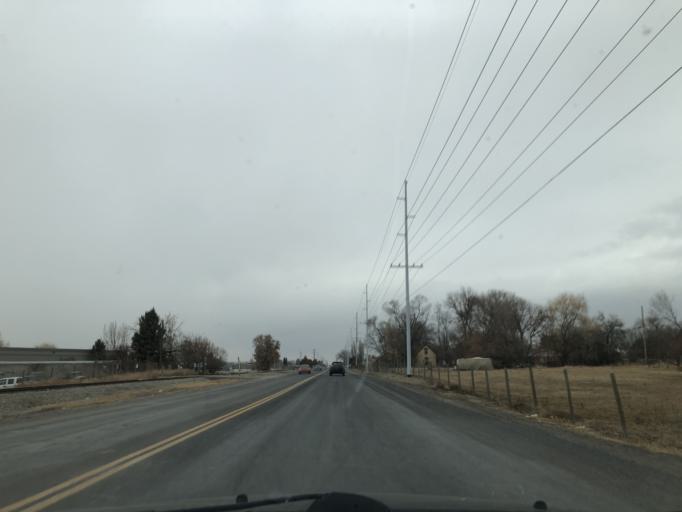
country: US
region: Utah
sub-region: Cache County
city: Logan
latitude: 41.7374
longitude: -111.8496
